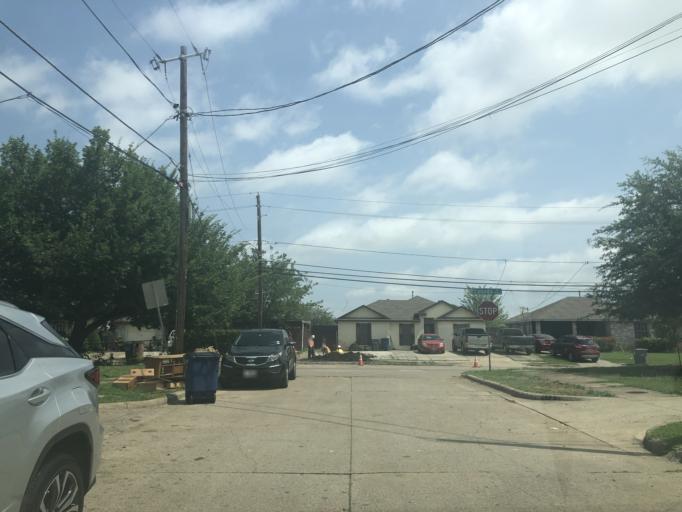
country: US
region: Texas
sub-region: Dallas County
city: Cockrell Hill
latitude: 32.7921
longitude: -96.8802
